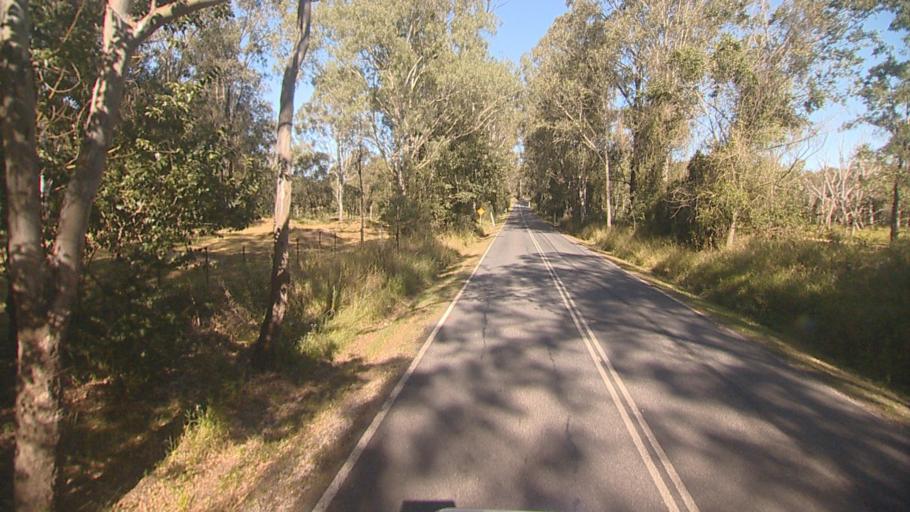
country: AU
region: Queensland
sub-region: Logan
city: Waterford West
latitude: -27.7141
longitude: 153.1414
